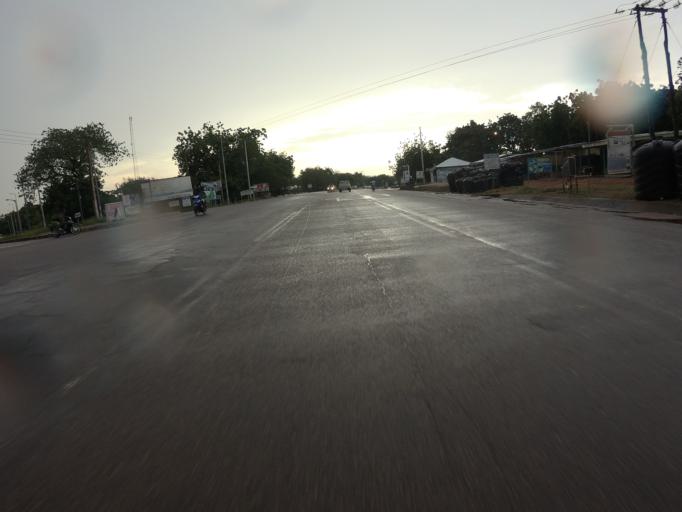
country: GH
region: Upper East
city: Bolgatanga
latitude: 10.8022
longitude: -0.8642
